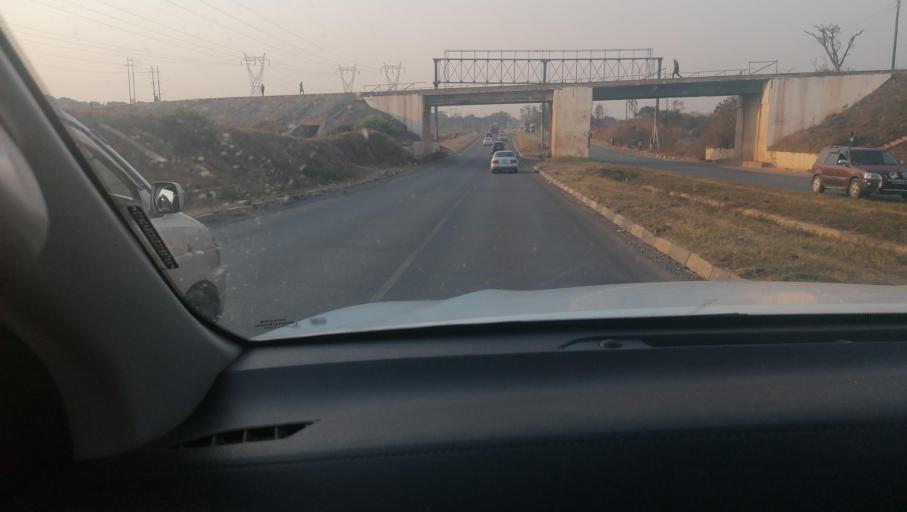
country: ZM
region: Copperbelt
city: Kitwe
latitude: -12.8391
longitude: 28.2143
